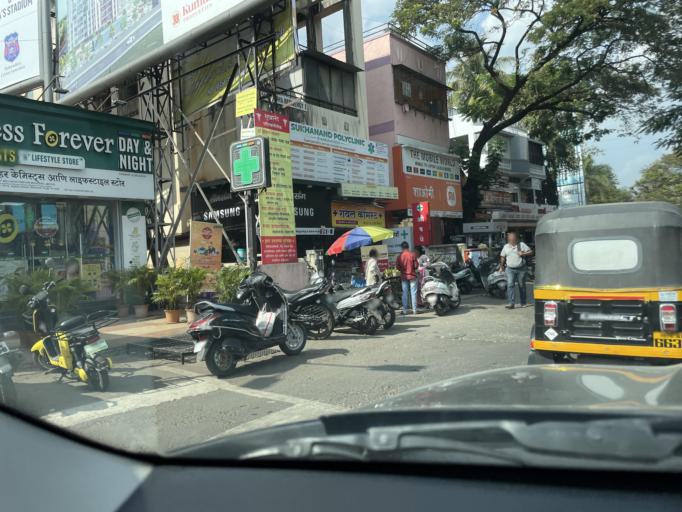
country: IN
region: Maharashtra
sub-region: Pune Division
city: Pune
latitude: 18.4922
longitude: 73.9000
